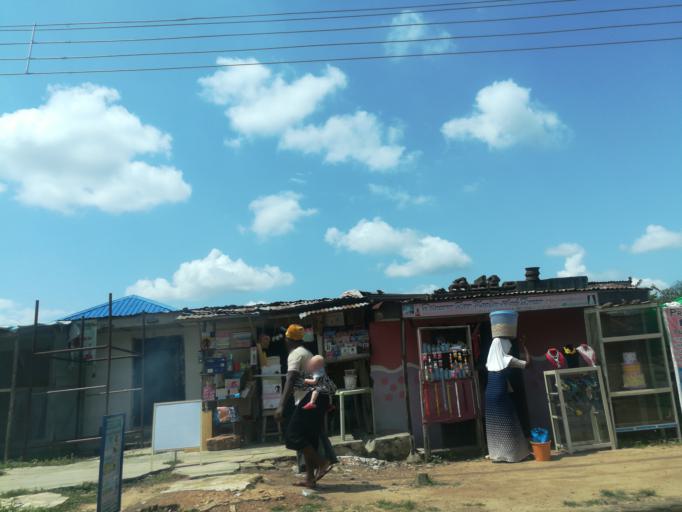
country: NG
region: Oyo
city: Egbeda
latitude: 7.4294
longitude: 4.0060
